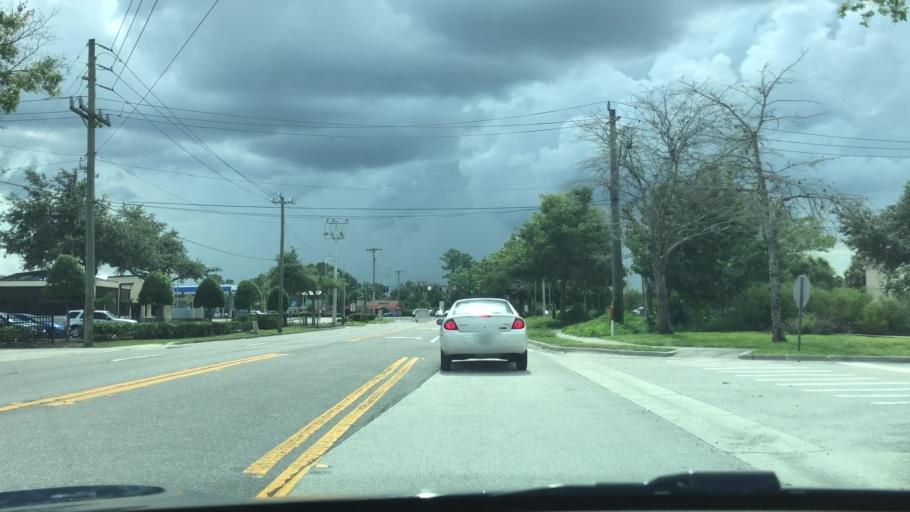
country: US
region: Florida
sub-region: Seminole County
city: Sanford
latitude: 28.7694
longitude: -81.2791
